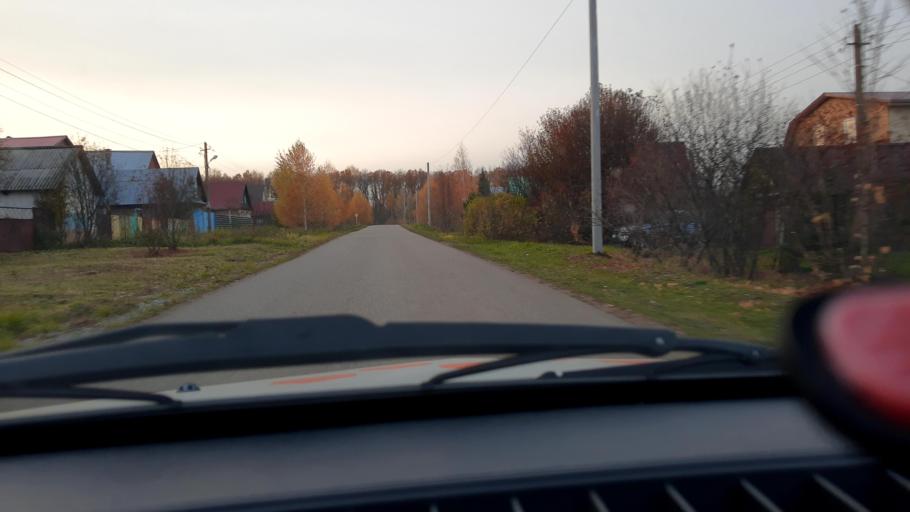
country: RU
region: Bashkortostan
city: Iglino
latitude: 54.7954
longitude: 56.3155
